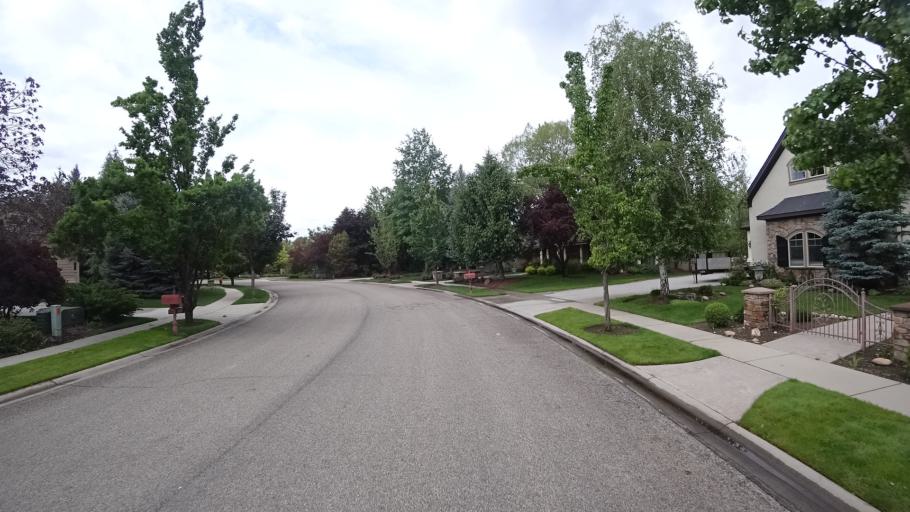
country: US
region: Idaho
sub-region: Ada County
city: Eagle
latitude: 43.6822
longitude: -116.3640
